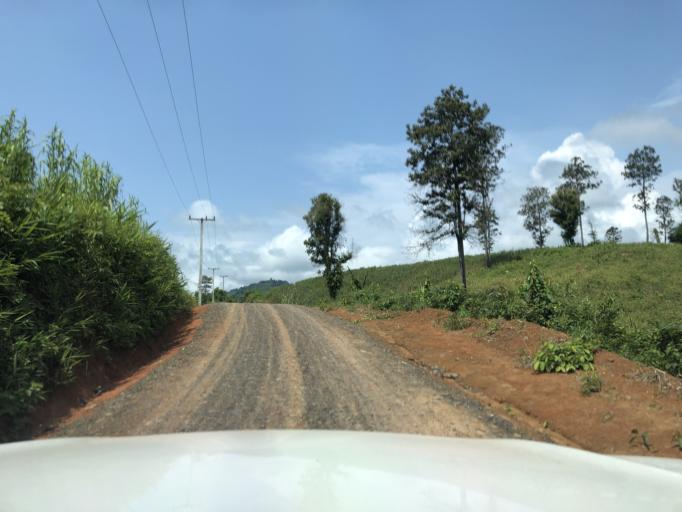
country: LA
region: Xiagnabouli
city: Sainyabuli
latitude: 19.0512
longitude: 101.5008
